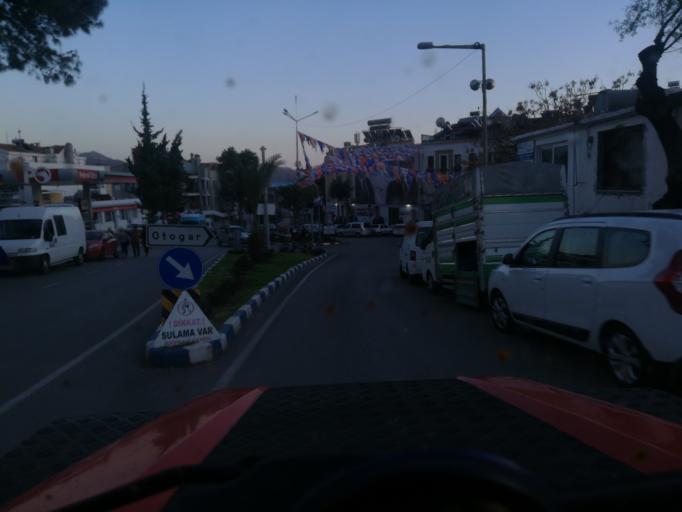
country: TR
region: Antalya
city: Kas
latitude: 36.2022
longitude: 29.6381
